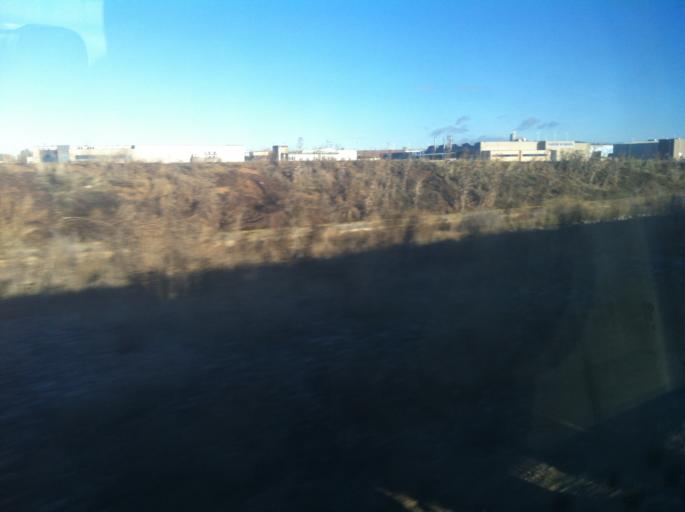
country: ES
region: Castille and Leon
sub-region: Provincia de Palencia
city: Venta de Banos
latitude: 41.9294
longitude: -4.4820
